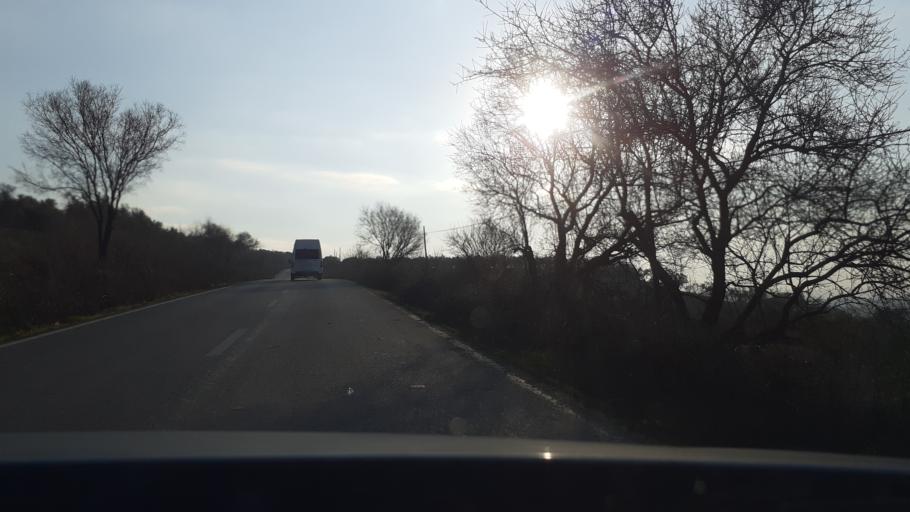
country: TR
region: Hatay
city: Oymakli
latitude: 36.1247
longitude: 36.3090
